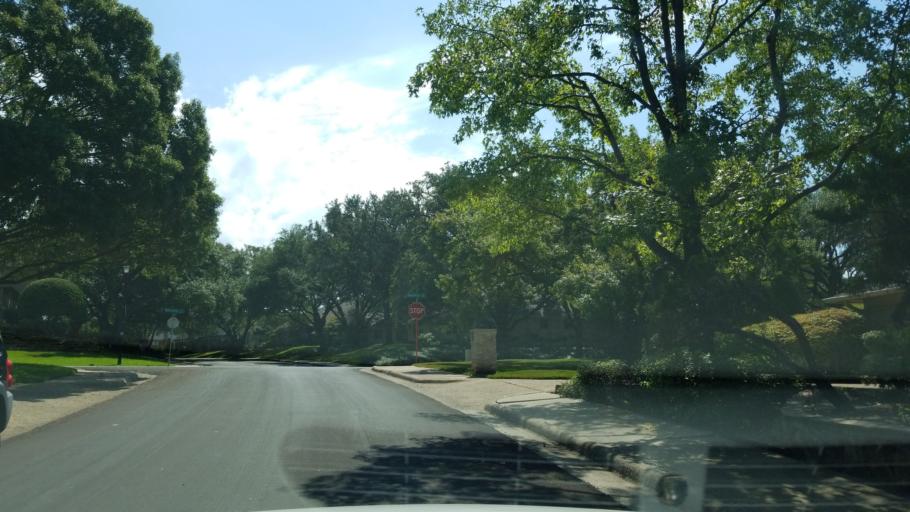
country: US
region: Texas
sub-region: Dallas County
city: Addison
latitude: 32.9648
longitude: -96.8017
